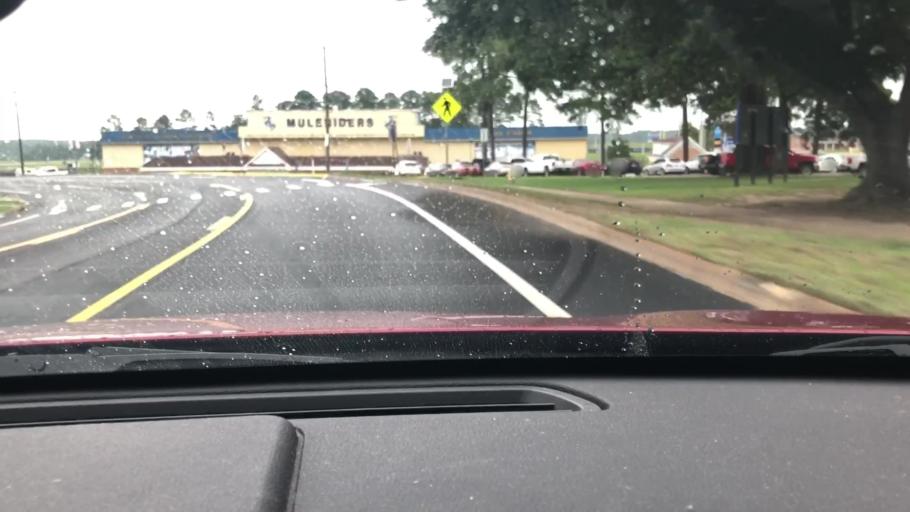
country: US
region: Arkansas
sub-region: Columbia County
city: Magnolia
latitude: 33.2934
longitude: -93.2366
